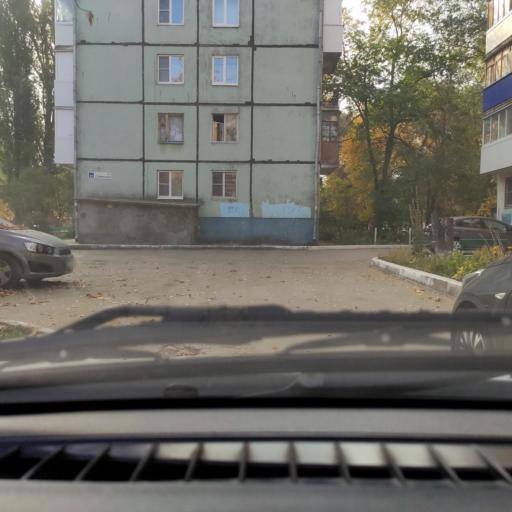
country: RU
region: Samara
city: Tol'yatti
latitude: 53.5012
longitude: 49.4068
